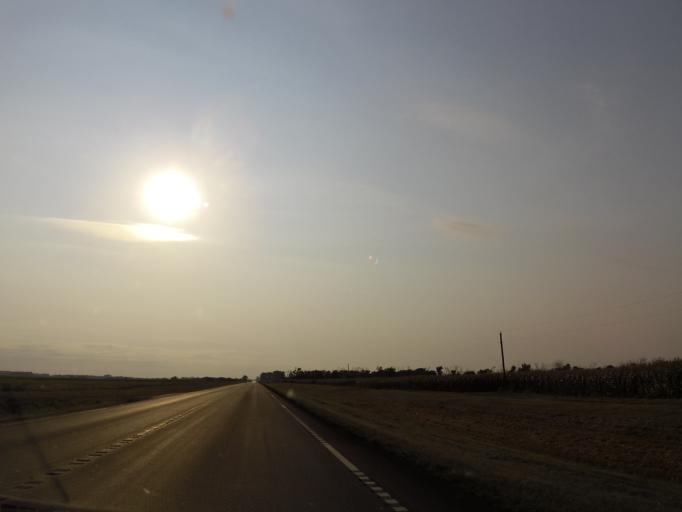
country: US
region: North Dakota
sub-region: Traill County
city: Mayville
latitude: 47.3529
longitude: -97.2874
